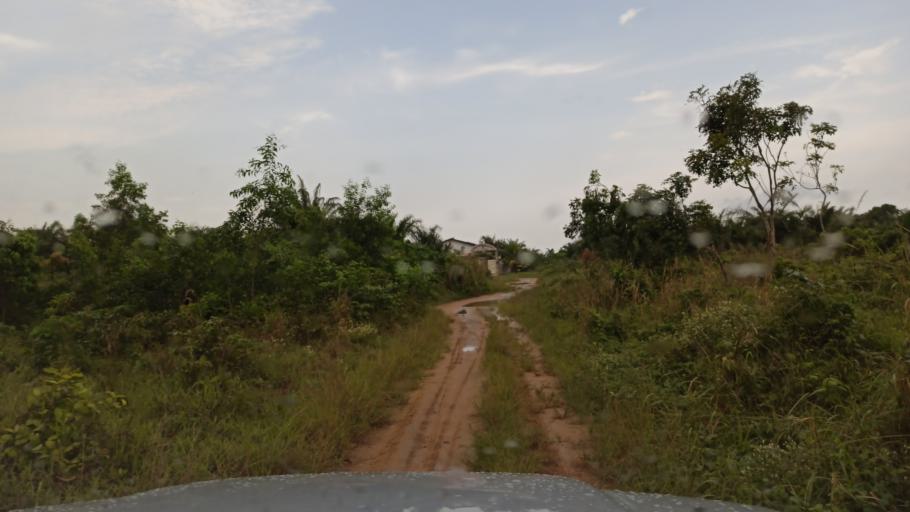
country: BJ
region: Queme
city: Porto-Novo
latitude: 6.4537
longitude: 2.6687
